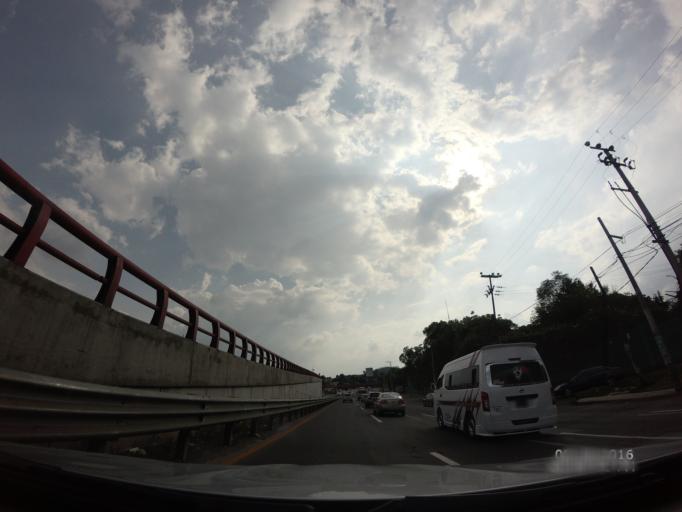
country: MX
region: Mexico
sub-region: Tlalnepantla de Baz
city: Puerto Escondido (Tepeolulco Puerto Escondido)
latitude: 19.5225
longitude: -99.0907
